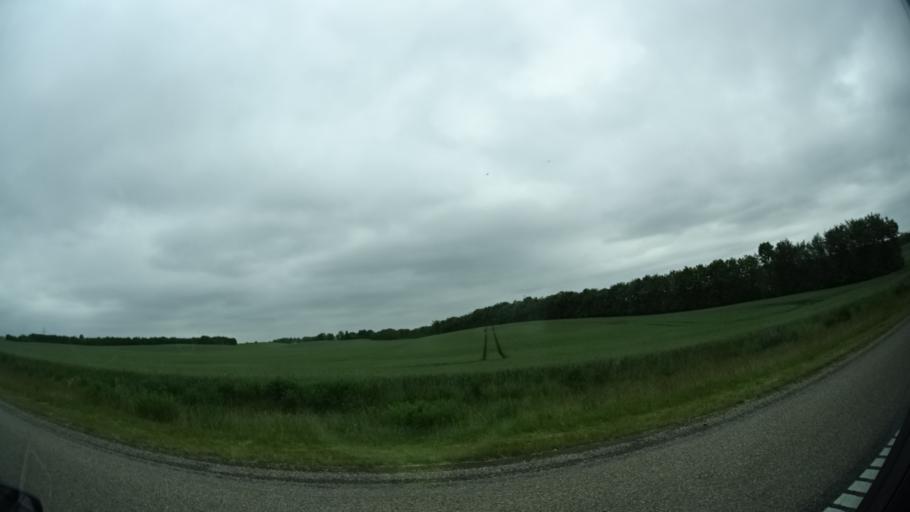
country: DK
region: Central Jutland
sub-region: Arhus Kommune
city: Trige
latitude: 56.2225
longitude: 10.1265
